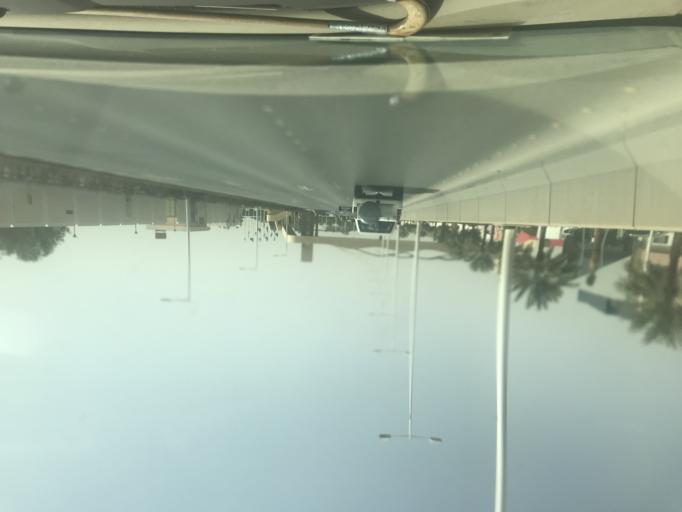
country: SA
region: Ar Riyad
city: Riyadh
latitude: 24.7343
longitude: 46.7080
